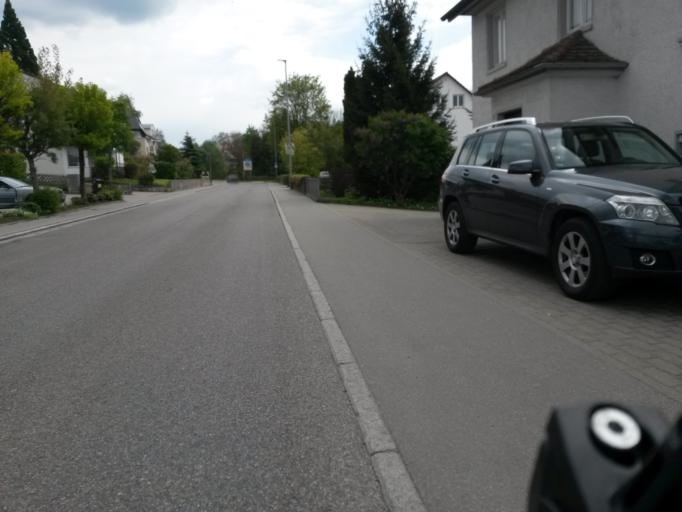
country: DE
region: Baden-Wuerttemberg
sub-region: Tuebingen Region
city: Bad Waldsee
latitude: 47.9238
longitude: 9.7454
